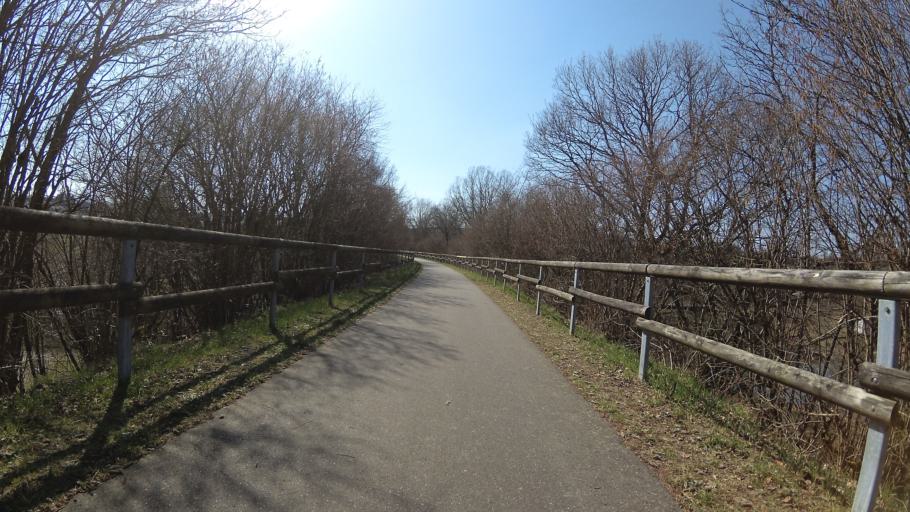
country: DE
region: Rheinland-Pfalz
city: Reinsfeld
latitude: 49.6788
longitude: 6.8812
